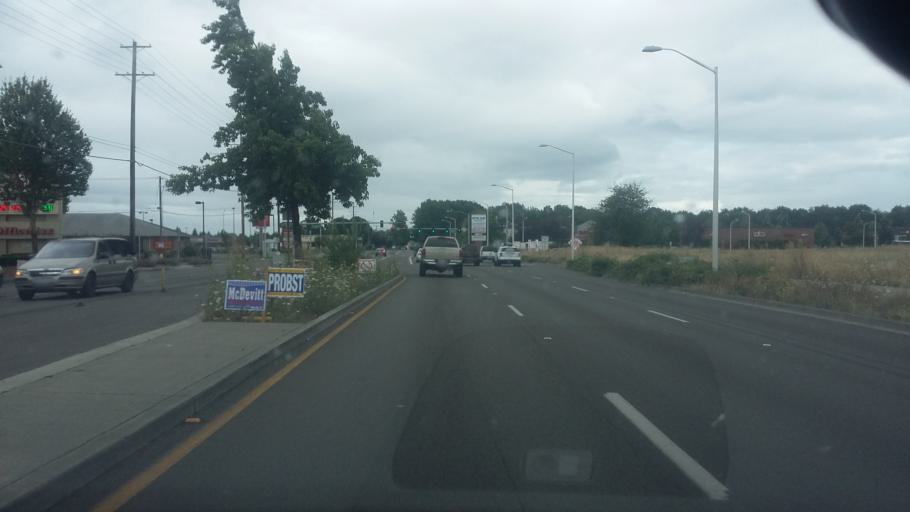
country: US
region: Washington
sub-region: Clark County
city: Mill Plain
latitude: 45.6184
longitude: -122.5302
